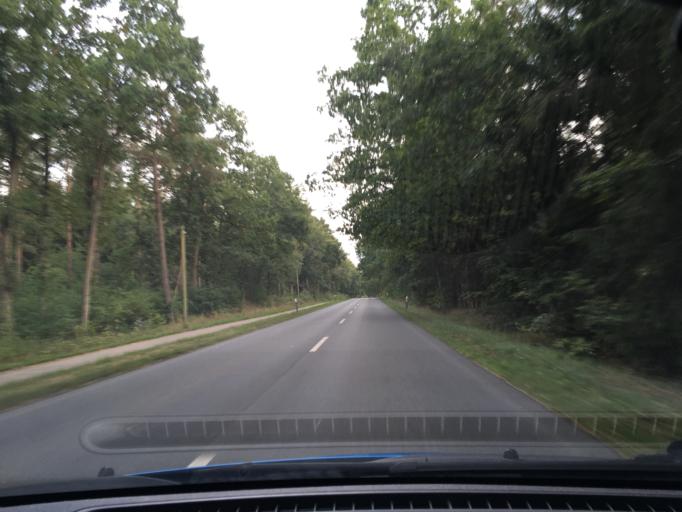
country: DE
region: Lower Saxony
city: Westergellersen
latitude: 53.2446
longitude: 10.2346
